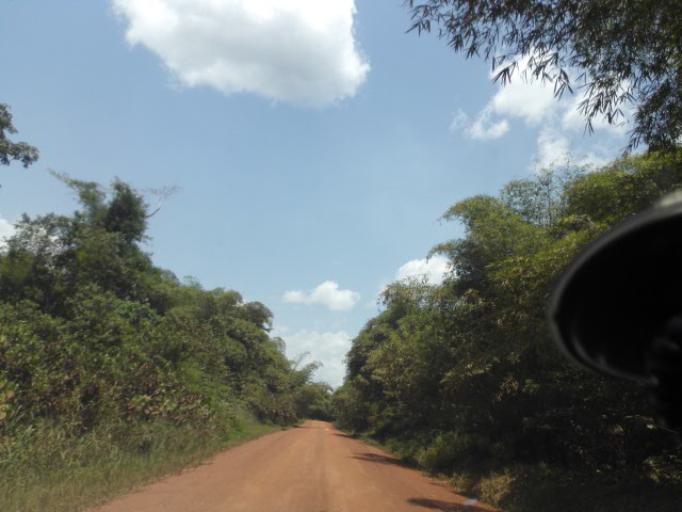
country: CD
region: Eastern Province
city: Kisangani
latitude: 0.6299
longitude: 26.0770
